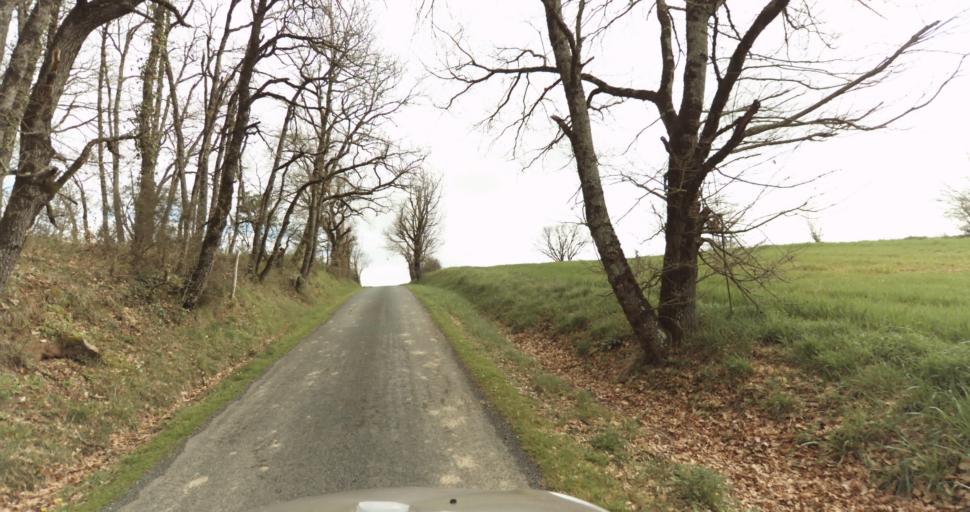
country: FR
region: Midi-Pyrenees
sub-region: Departement du Tarn
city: Frejairolles
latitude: 43.8820
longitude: 2.1991
